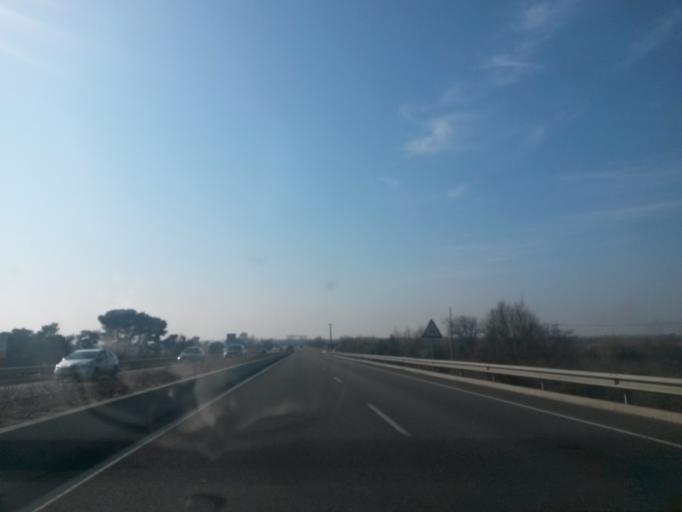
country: ES
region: Catalonia
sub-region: Provincia de Girona
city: Empuriabrava
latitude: 42.2712
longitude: 3.1324
